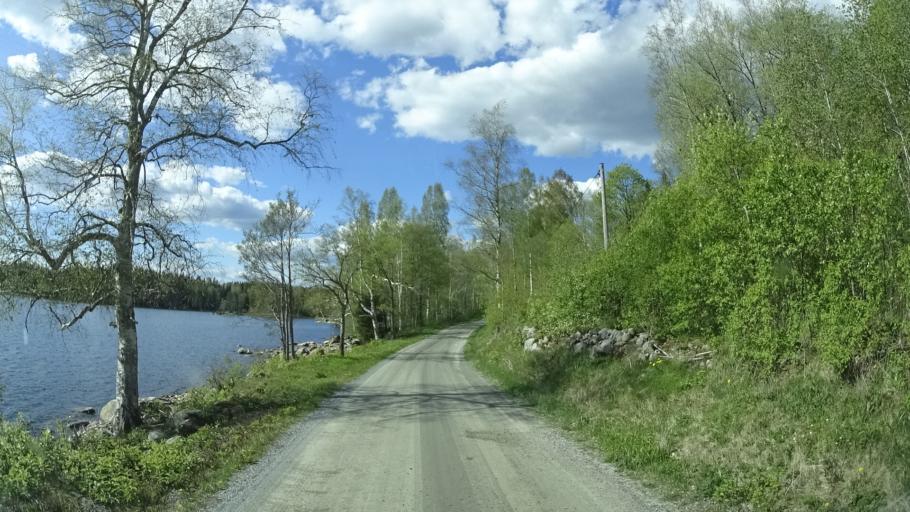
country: SE
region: OErebro
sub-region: Nora Kommun
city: As
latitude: 59.4473
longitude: 14.8102
